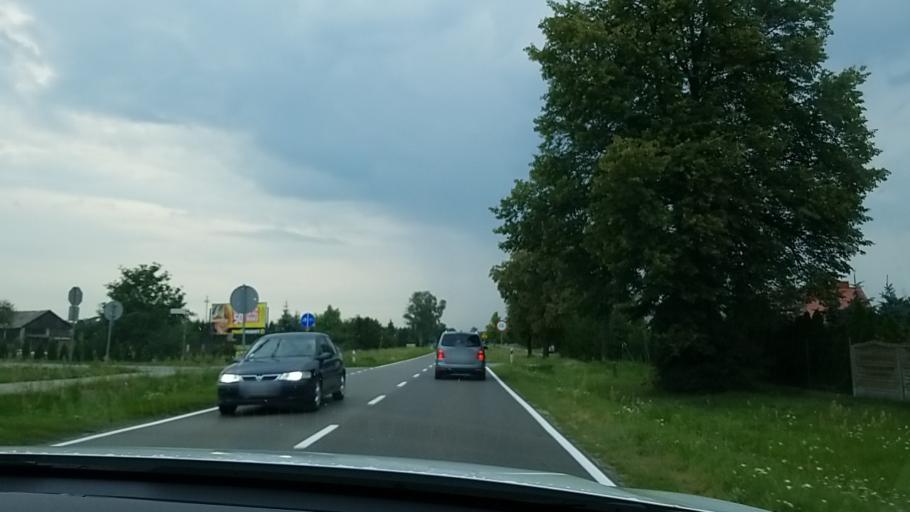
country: PL
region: Lublin Voivodeship
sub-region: Powiat wlodawski
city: Wlodawa
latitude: 51.5620
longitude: 23.5512
